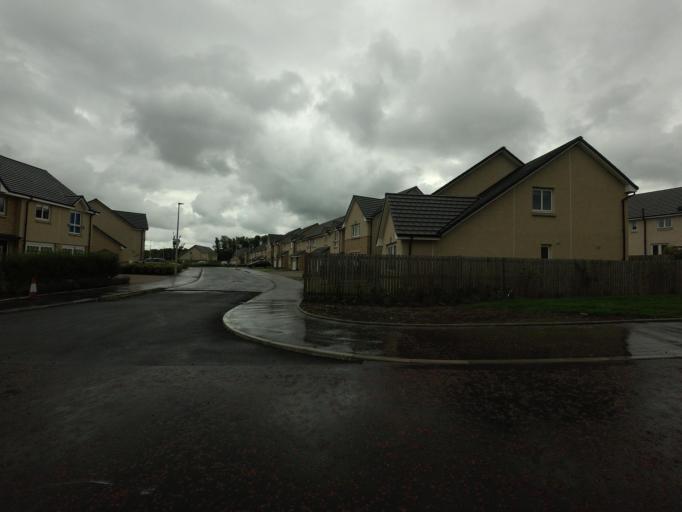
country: GB
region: Scotland
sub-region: West Lothian
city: West Calder
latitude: 55.8583
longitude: -3.5733
